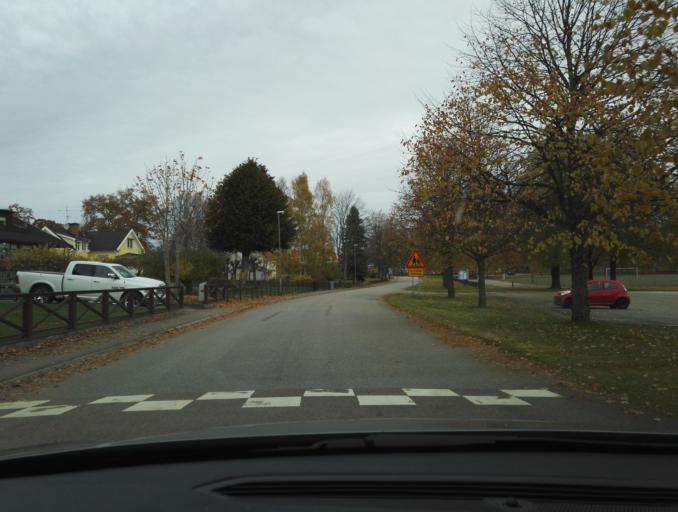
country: SE
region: Kronoberg
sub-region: Vaxjo Kommun
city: Vaexjoe
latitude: 56.9090
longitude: 14.7419
